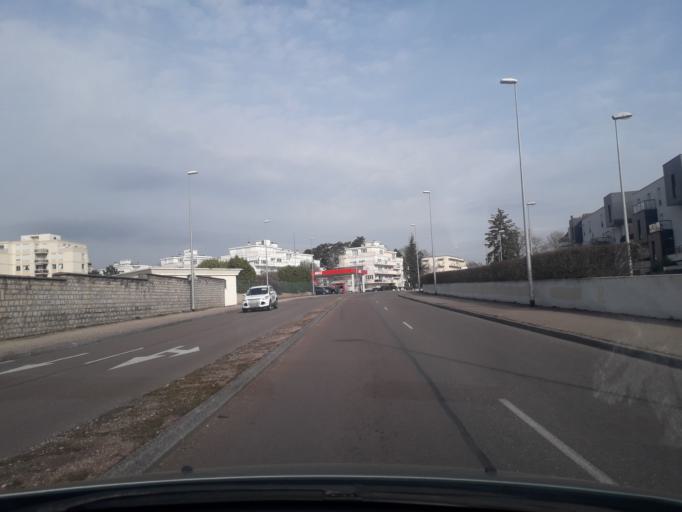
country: FR
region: Bourgogne
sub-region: Departement de la Cote-d'Or
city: Talant
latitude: 47.3284
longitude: 5.0135
